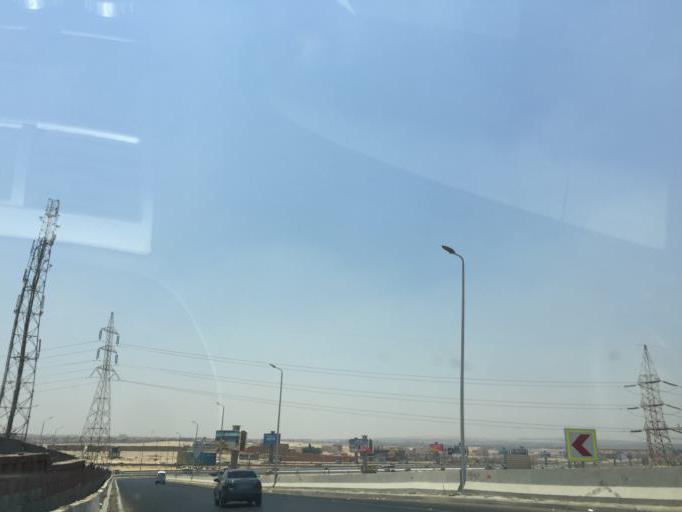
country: EG
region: Al Jizah
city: Awsim
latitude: 30.0491
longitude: 31.0539
